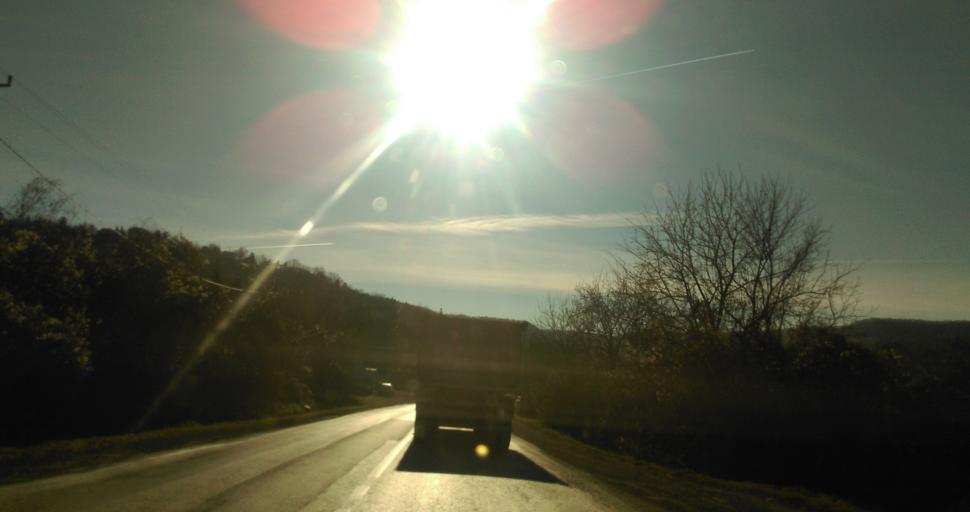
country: RS
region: Autonomna Pokrajina Vojvodina
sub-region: Juznobacki Okrug
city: Novi Sad
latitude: 45.2017
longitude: 19.8424
